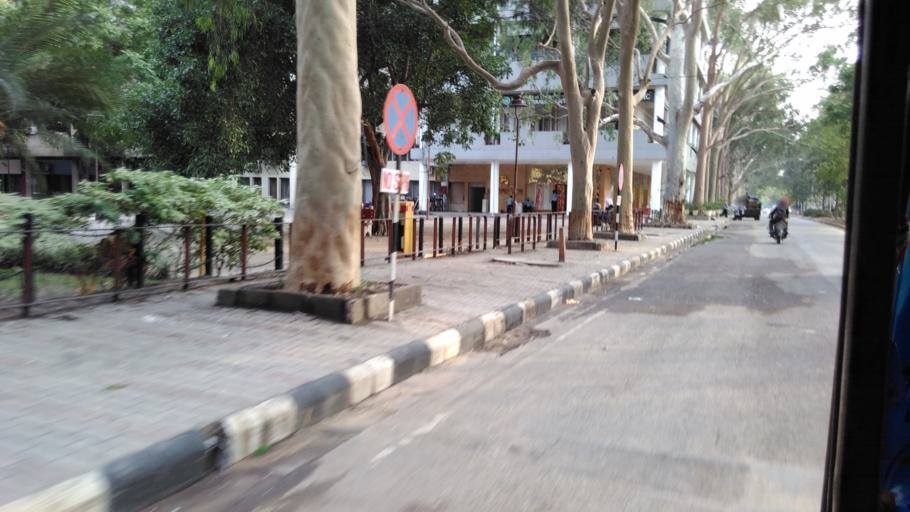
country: IN
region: Chandigarh
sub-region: Chandigarh
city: Chandigarh
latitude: 30.7451
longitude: 76.7842
